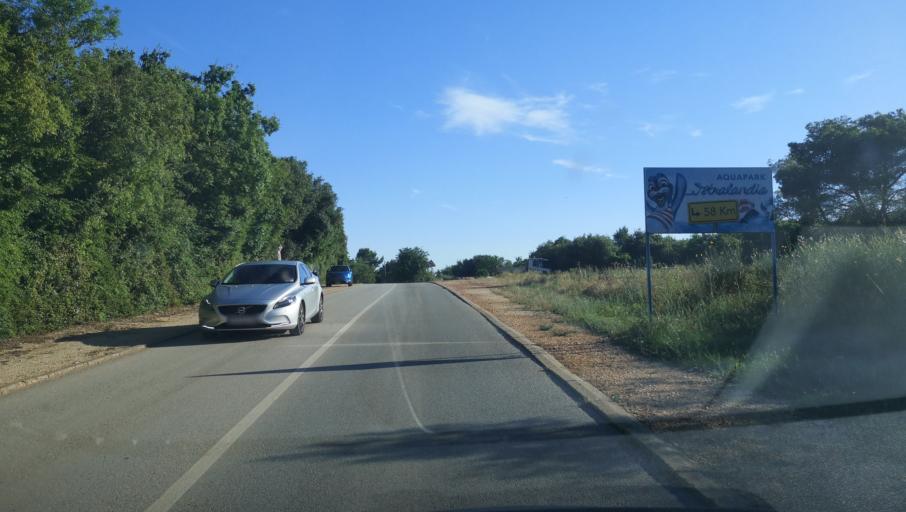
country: HR
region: Istarska
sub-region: Grad Rovinj
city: Rovinj
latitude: 45.0568
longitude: 13.6871
